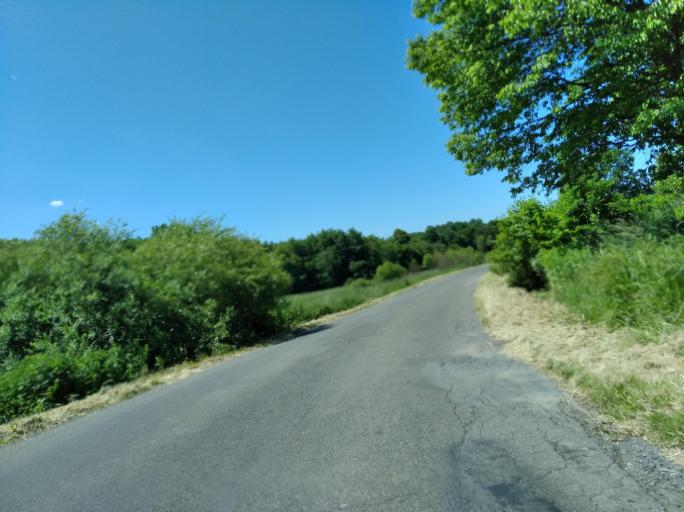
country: PL
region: Subcarpathian Voivodeship
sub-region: Powiat krosnienski
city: Chorkowka
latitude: 49.6414
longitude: 21.6360
